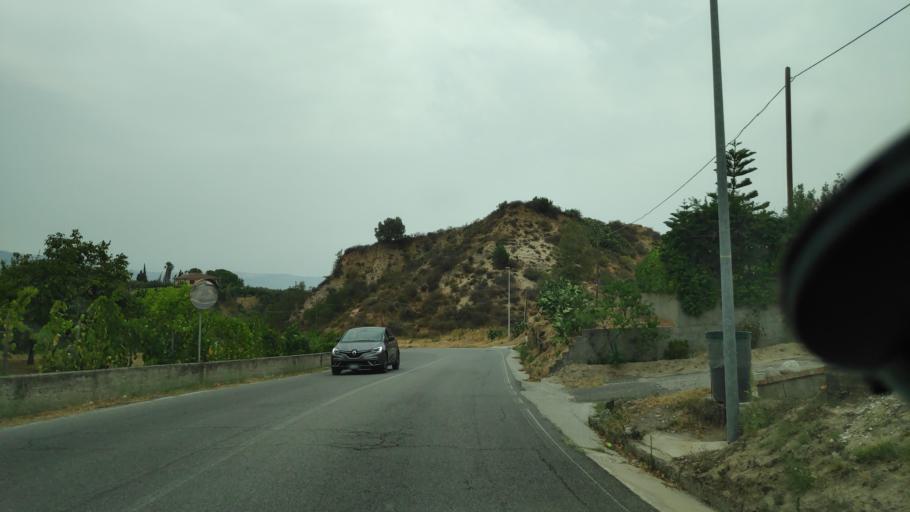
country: IT
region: Calabria
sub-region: Provincia di Catanzaro
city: Davoli
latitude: 38.6645
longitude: 16.5064
